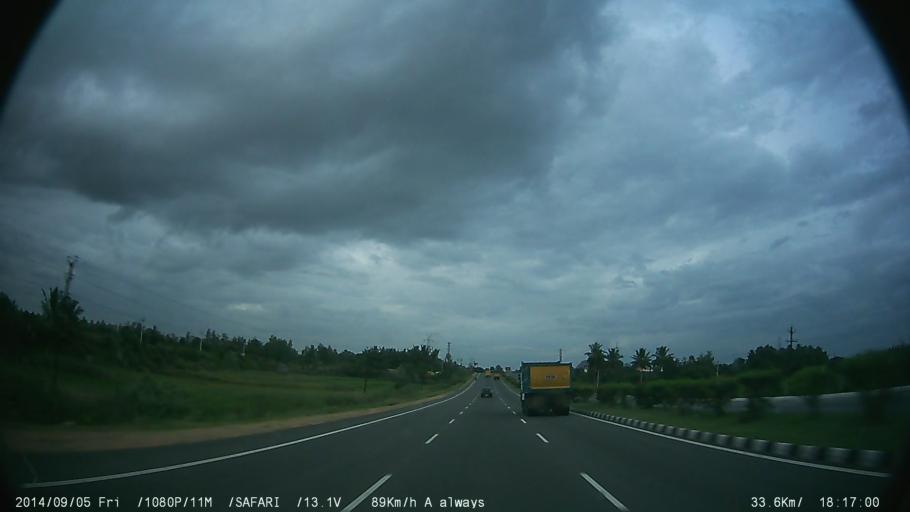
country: IN
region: Tamil Nadu
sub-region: Krishnagiri
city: Kelamangalam
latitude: 12.6711
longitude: 77.9760
